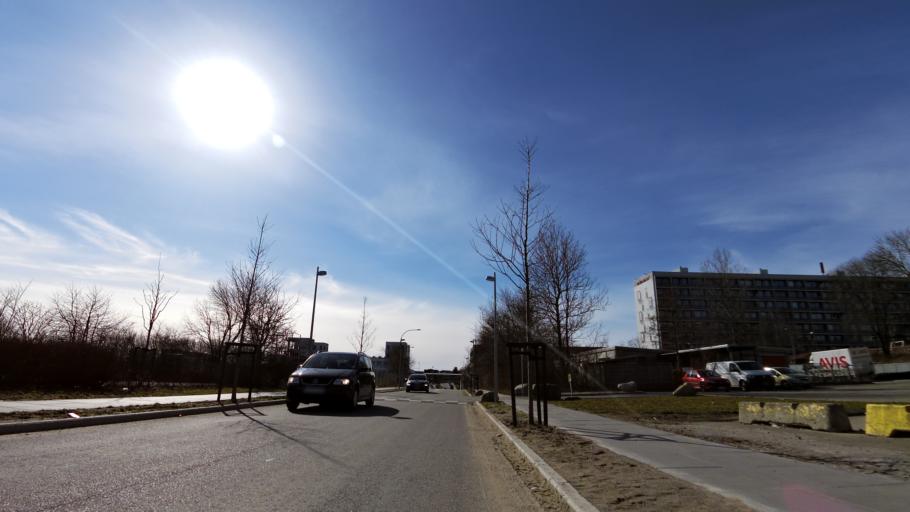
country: DK
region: Central Jutland
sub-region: Arhus Kommune
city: Stavtrup
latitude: 56.1559
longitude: 10.1389
